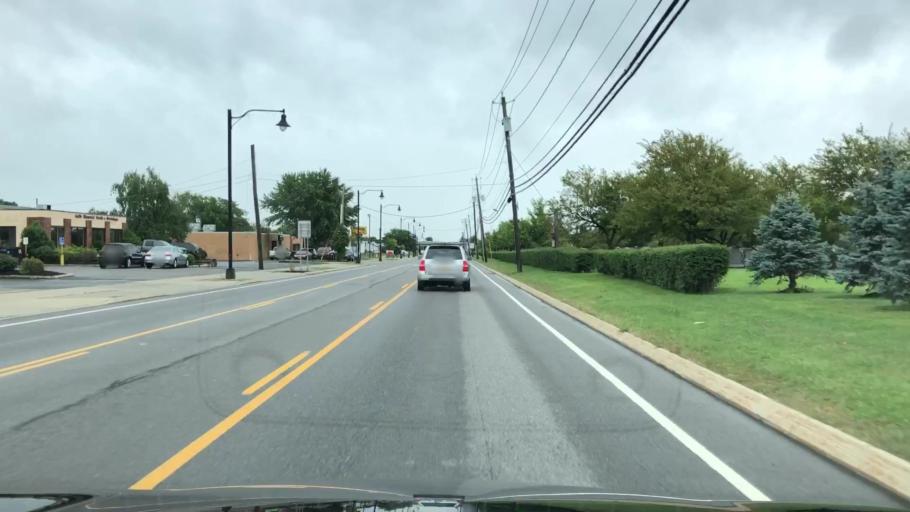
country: US
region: New York
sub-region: Erie County
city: Eggertsville
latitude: 42.9371
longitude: -78.7842
